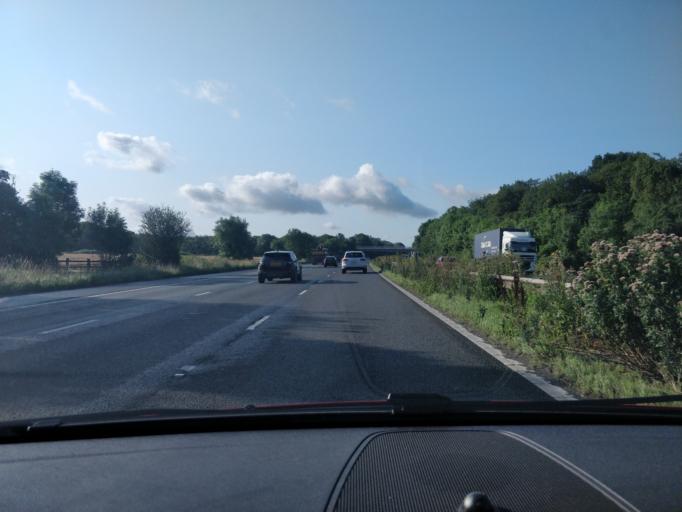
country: GB
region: England
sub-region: Knowsley
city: Knowsley
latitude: 53.4487
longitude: -2.8620
